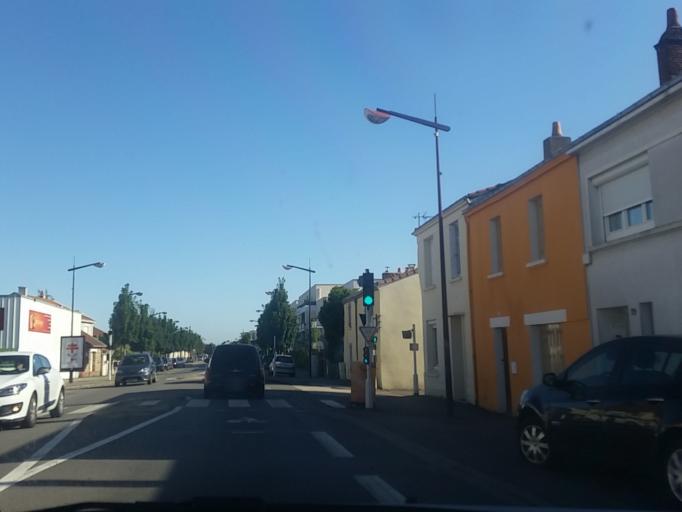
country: FR
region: Pays de la Loire
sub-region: Departement de la Loire-Atlantique
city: Reze
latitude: 47.1745
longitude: -1.5437
